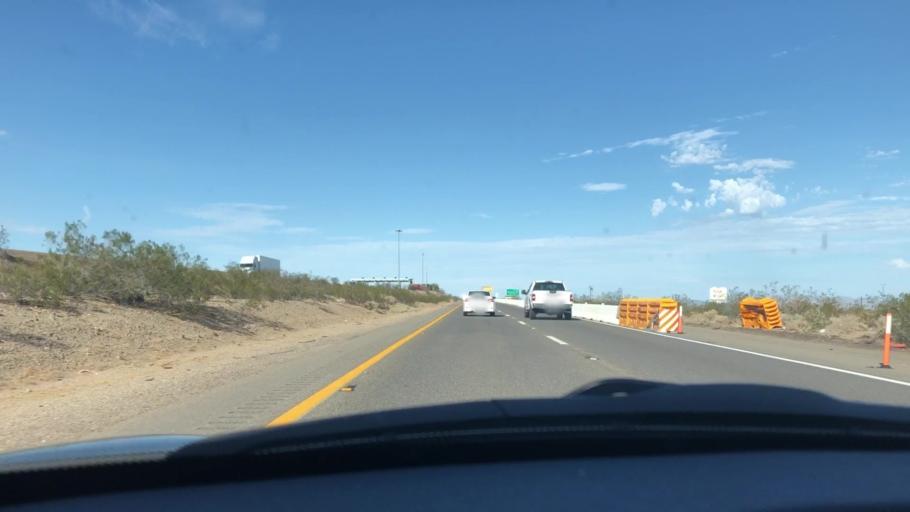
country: US
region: California
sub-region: San Bernardino County
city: Barstow
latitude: 34.9127
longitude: -116.7965
